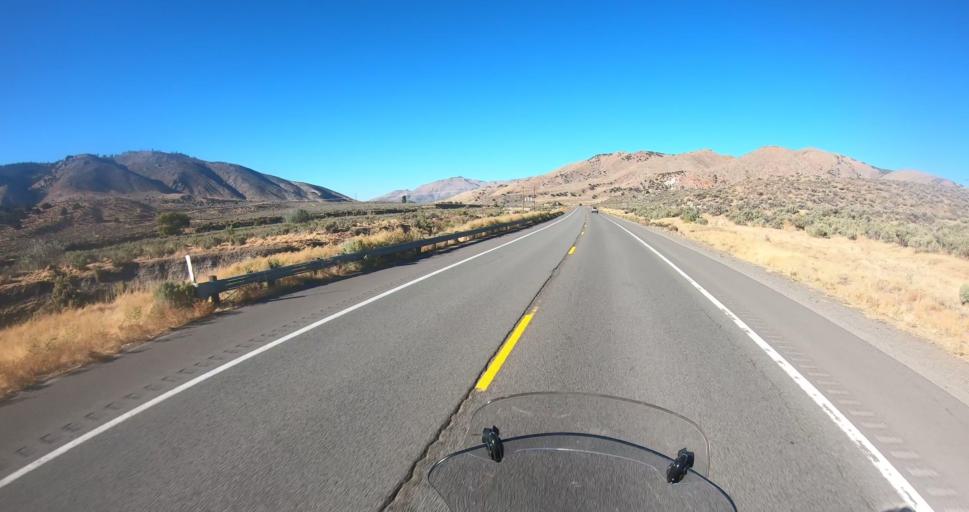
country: US
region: Nevada
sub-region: Washoe County
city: Cold Springs
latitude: 39.8990
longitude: -120.0157
